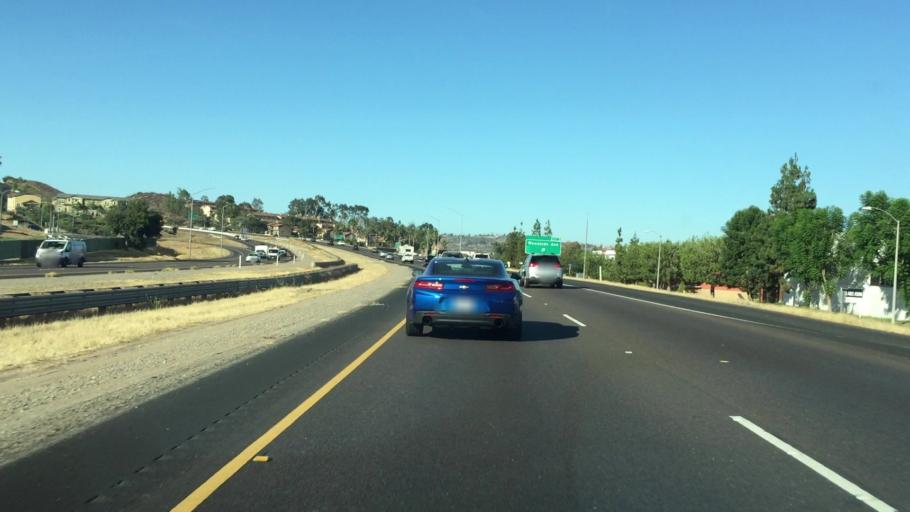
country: US
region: California
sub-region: San Diego County
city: Santee
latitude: 32.8450
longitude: -116.9590
